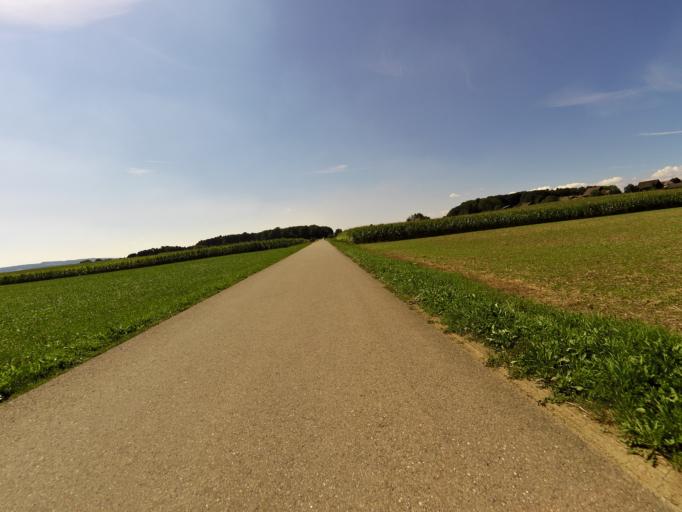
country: CH
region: Thurgau
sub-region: Kreuzlingen District
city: Ermatingen
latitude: 47.6295
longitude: 9.0923
